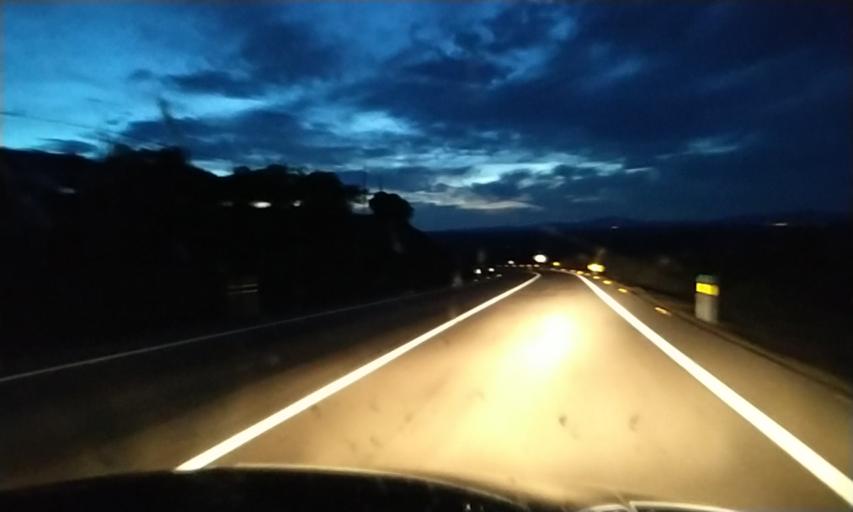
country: ES
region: Extremadura
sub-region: Provincia de Caceres
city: Galisteo
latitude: 39.9780
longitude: -6.2029
